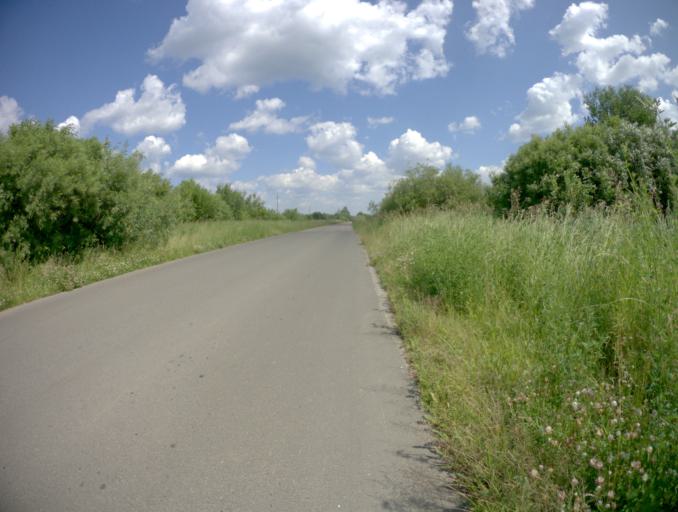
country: RU
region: Vladimir
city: Vyazniki
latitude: 56.3099
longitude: 42.1227
